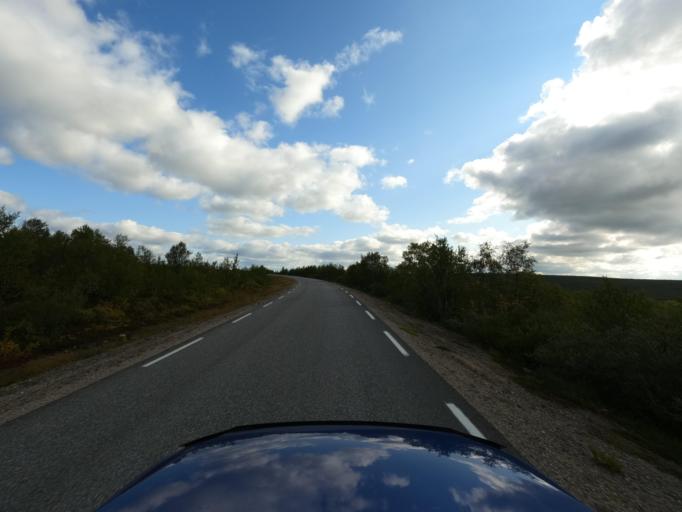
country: NO
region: Finnmark Fylke
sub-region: Porsanger
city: Lakselv
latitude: 69.3736
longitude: 24.4158
